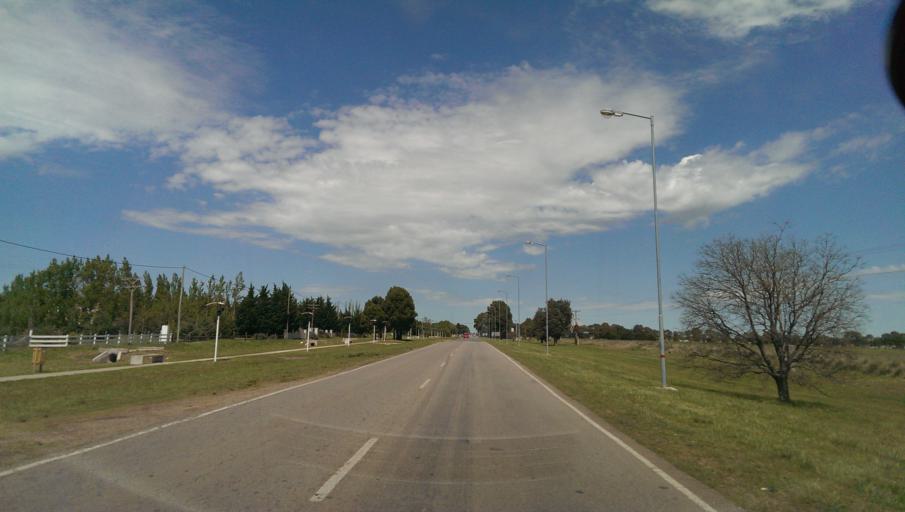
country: AR
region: Buenos Aires
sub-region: Partido de Tornquist
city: Tornquist
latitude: -38.0822
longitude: -62.2199
